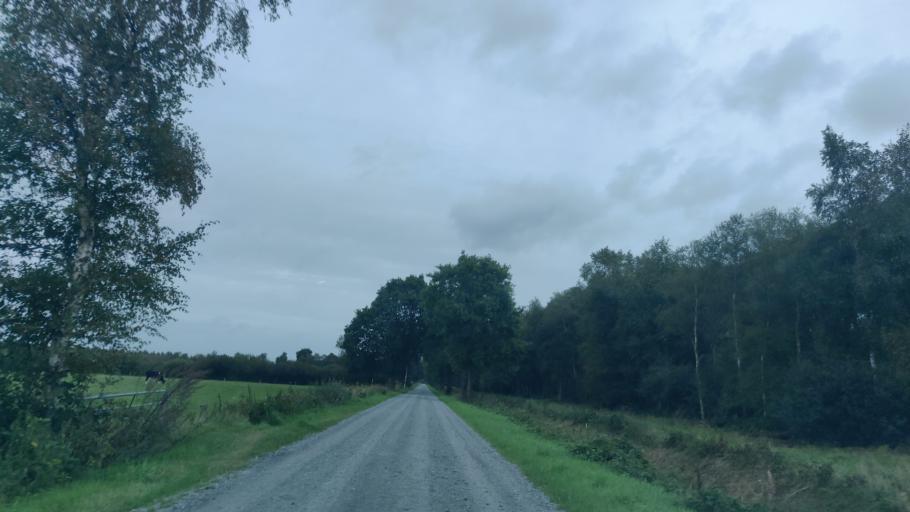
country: DE
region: Lower Saxony
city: Aurich
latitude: 53.5324
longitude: 7.4725
